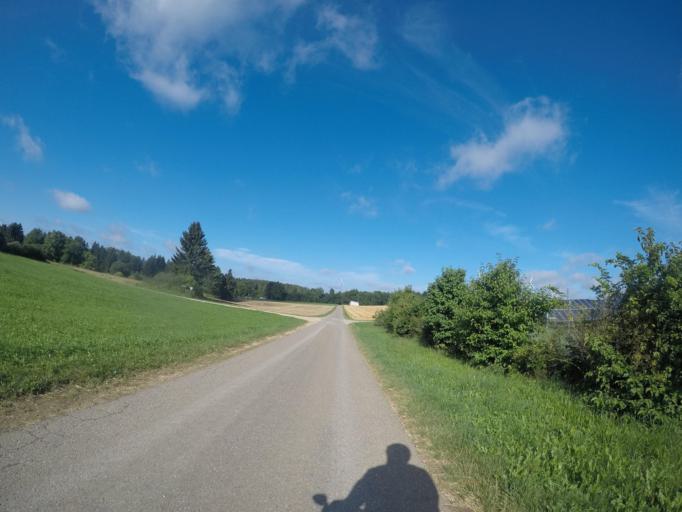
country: DE
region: Baden-Wuerttemberg
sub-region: Tuebingen Region
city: Mehrstetten
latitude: 48.3876
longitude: 9.6397
